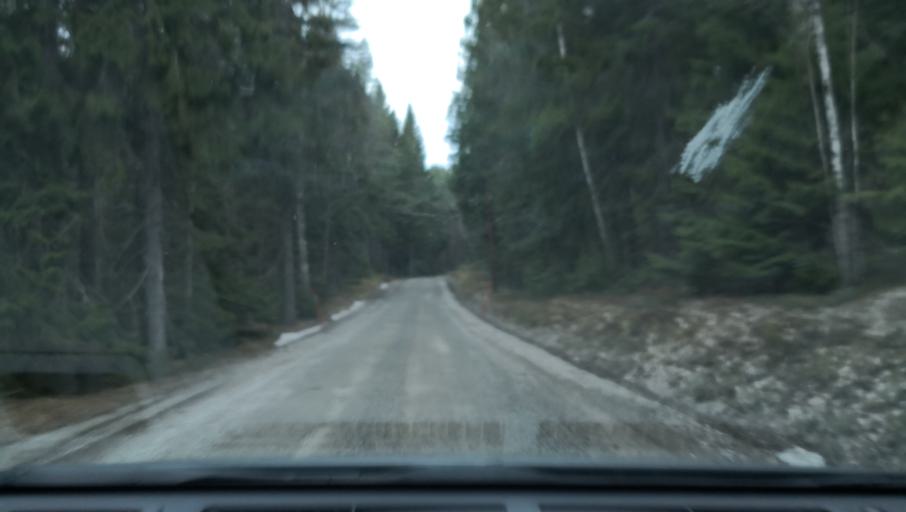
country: SE
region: Vaestmanland
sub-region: Kopings Kommun
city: Kolsva
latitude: 59.5771
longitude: 15.7128
